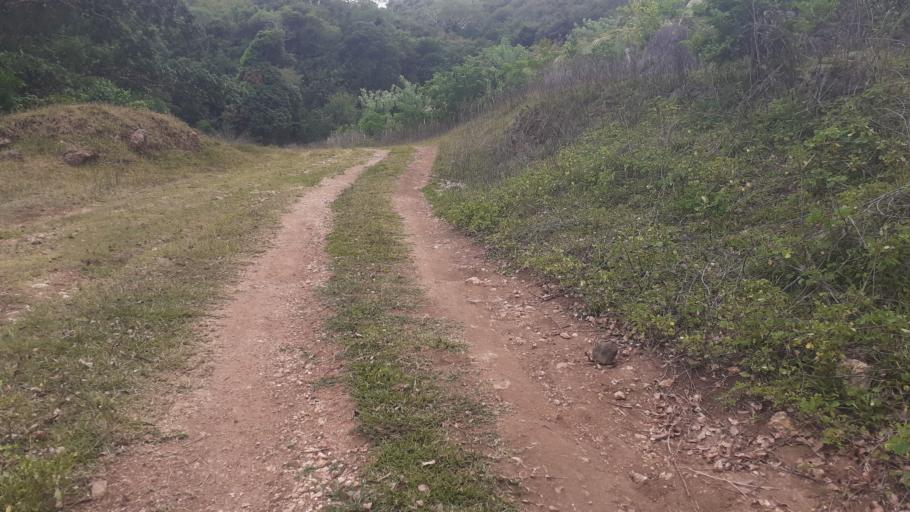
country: VU
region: Tafea
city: Isangel
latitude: -18.8198
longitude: 169.0234
